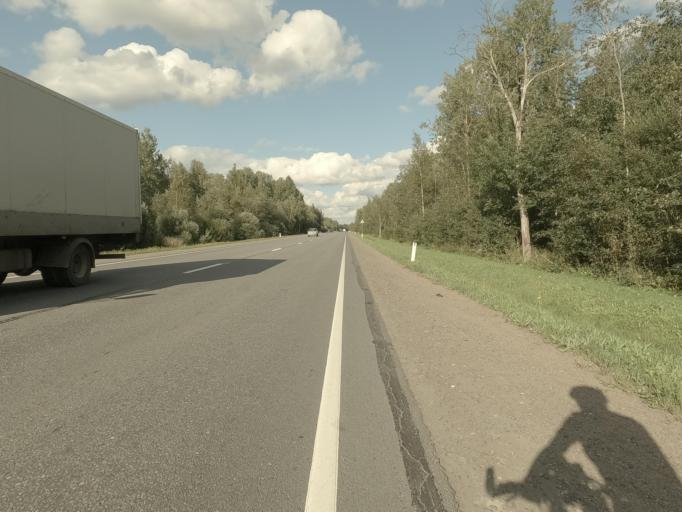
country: RU
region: Leningrad
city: Nikol'skoye
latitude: 59.6567
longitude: 30.8639
